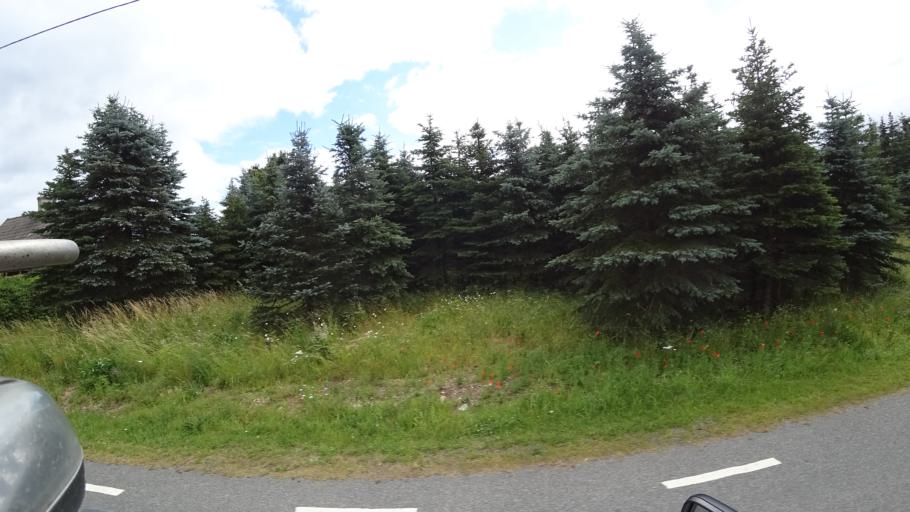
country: SE
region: Skane
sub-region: Kristianstads Kommun
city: Degeberga
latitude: 55.7274
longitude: 13.9999
